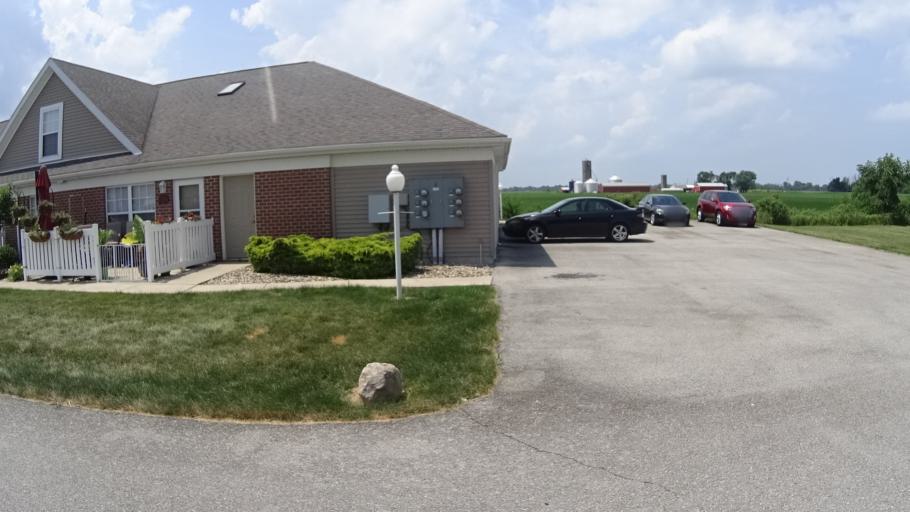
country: US
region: Ohio
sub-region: Lorain County
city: Vermilion
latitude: 41.4068
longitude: -82.3716
